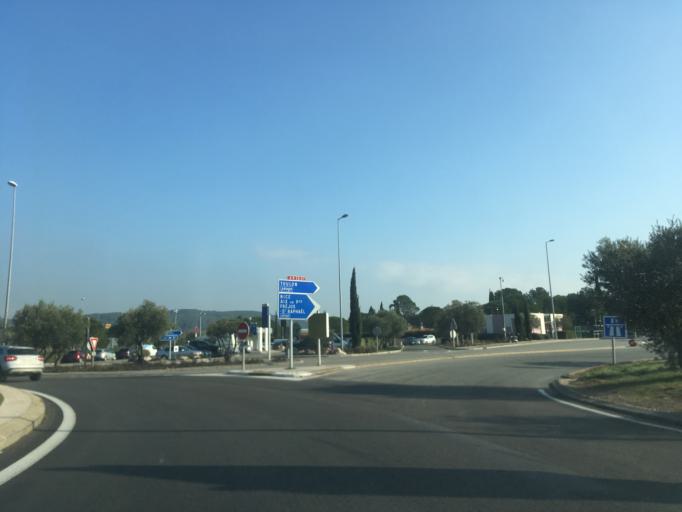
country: FR
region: Provence-Alpes-Cote d'Azur
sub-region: Departement du Var
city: Le Cannet-des-Maures
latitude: 43.3936
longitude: 6.3508
